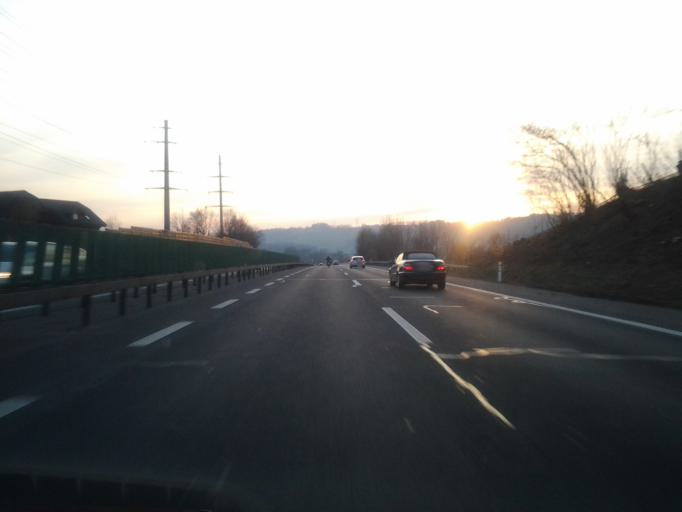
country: CH
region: Zug
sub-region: Zug
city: Hunenberg
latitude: 47.1457
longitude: 8.4194
